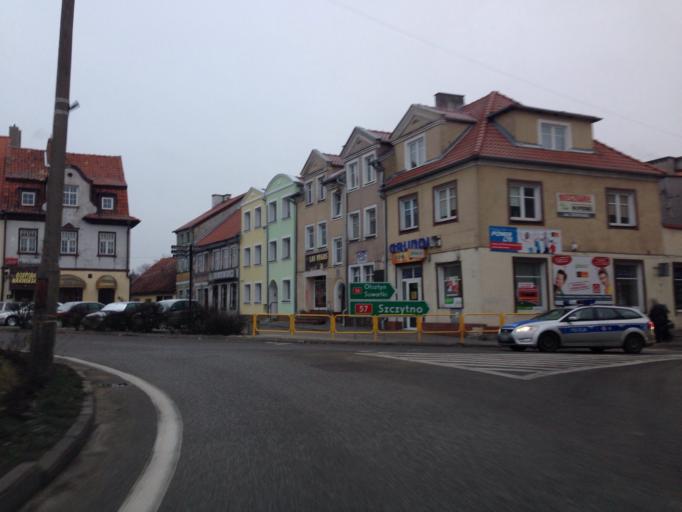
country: PL
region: Warmian-Masurian Voivodeship
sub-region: Powiat olsztynski
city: Biskupiec
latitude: 53.8629
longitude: 20.9560
